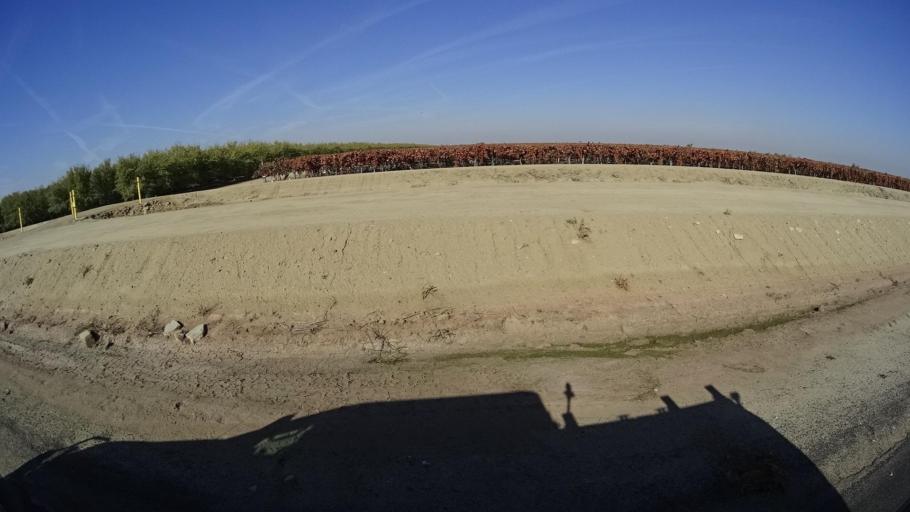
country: US
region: California
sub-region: Kern County
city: Wasco
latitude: 35.6454
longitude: -119.2940
